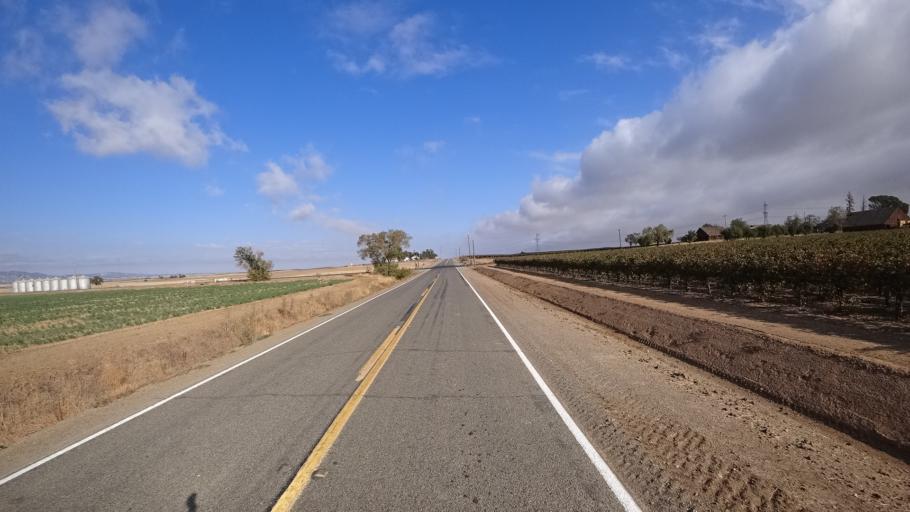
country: US
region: California
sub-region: Yolo County
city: Esparto
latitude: 38.7799
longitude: -122.0072
